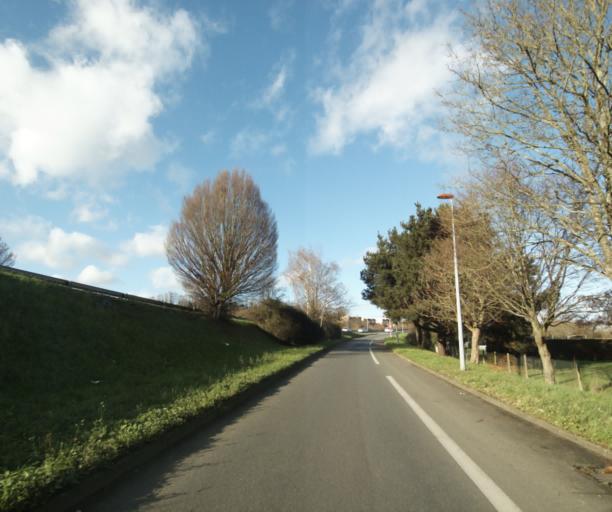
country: FR
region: Pays de la Loire
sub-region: Departement de la Sarthe
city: Le Mans
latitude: 47.9936
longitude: 0.1730
